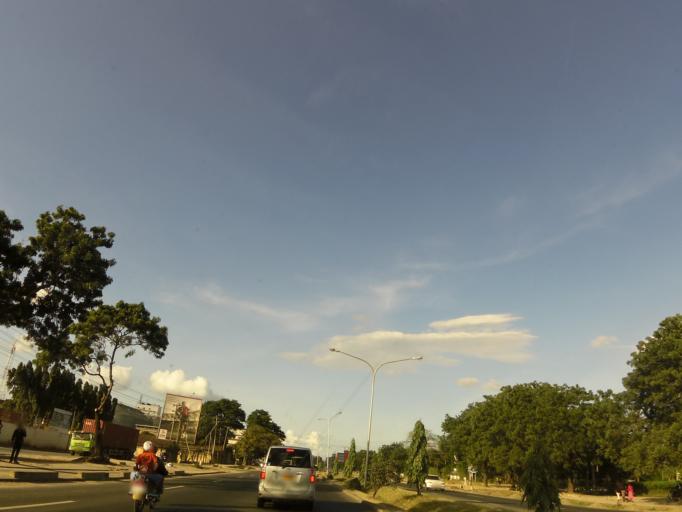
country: TZ
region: Dar es Salaam
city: Dar es Salaam
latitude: -6.8463
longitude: 39.2406
